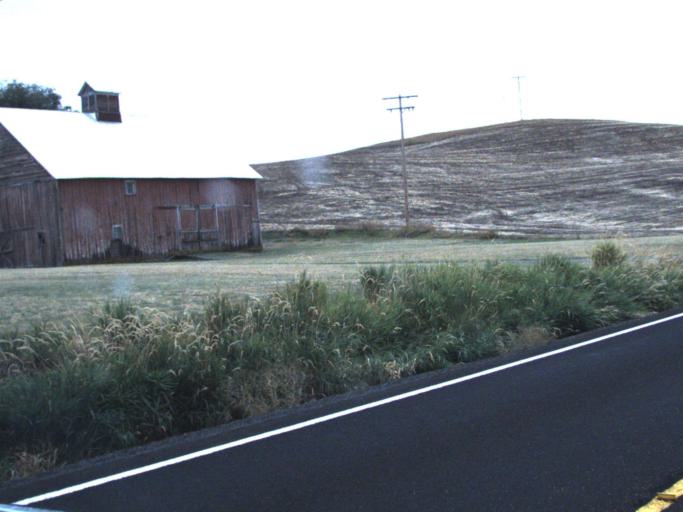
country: US
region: Washington
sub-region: Whitman County
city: Colfax
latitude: 47.1867
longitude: -117.3282
